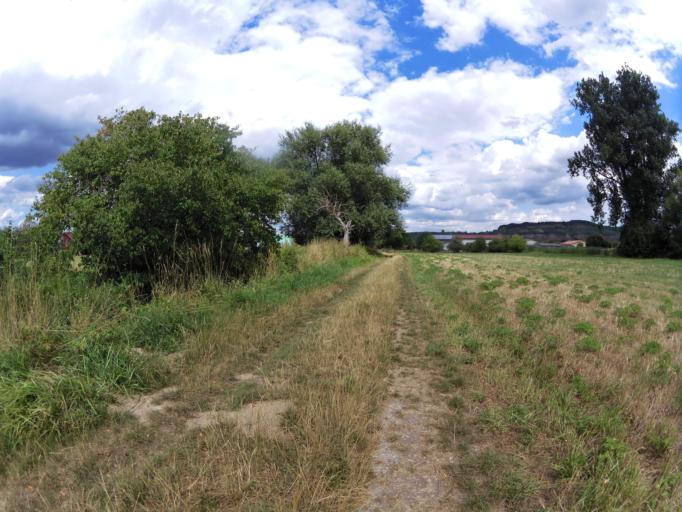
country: DE
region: Bavaria
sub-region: Regierungsbezirk Unterfranken
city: Zellingen
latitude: 49.8894
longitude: 9.8090
